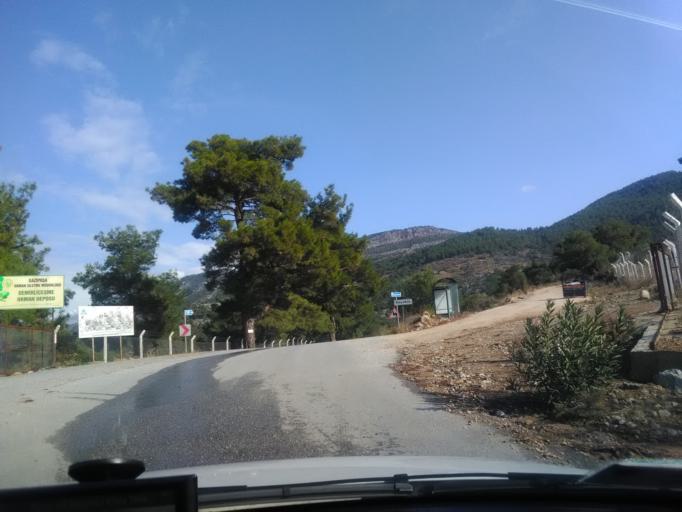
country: TR
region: Antalya
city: Gazipasa
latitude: 36.2976
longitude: 32.3357
